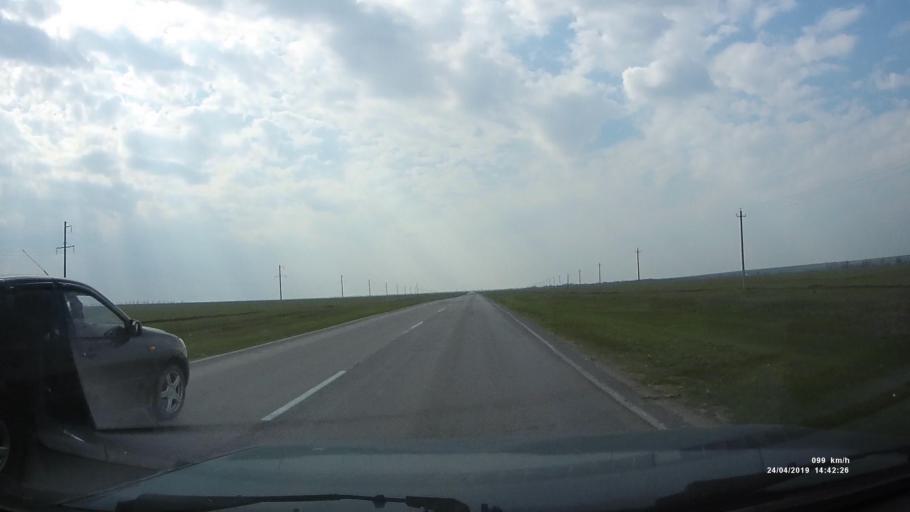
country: RU
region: Rostov
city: Remontnoye
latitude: 46.4520
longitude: 43.8620
